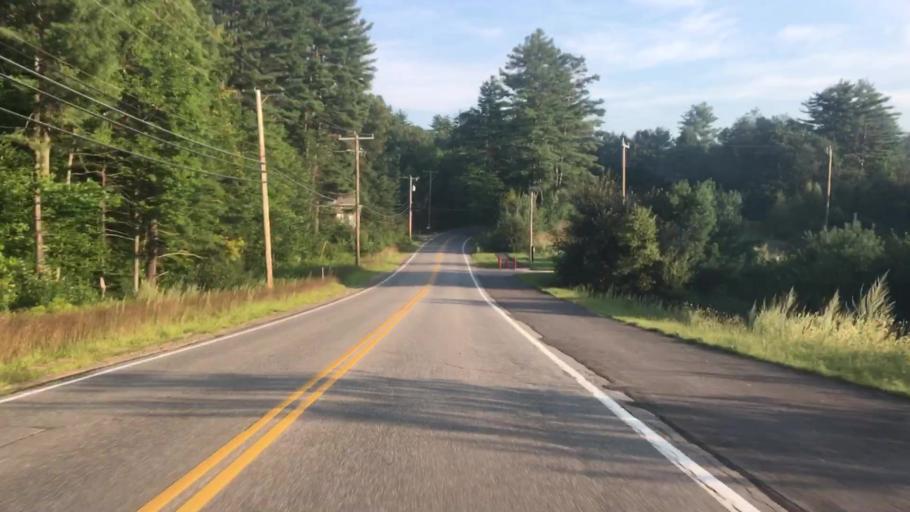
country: US
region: New Hampshire
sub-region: Belknap County
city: Laconia
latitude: 43.5079
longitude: -71.4502
